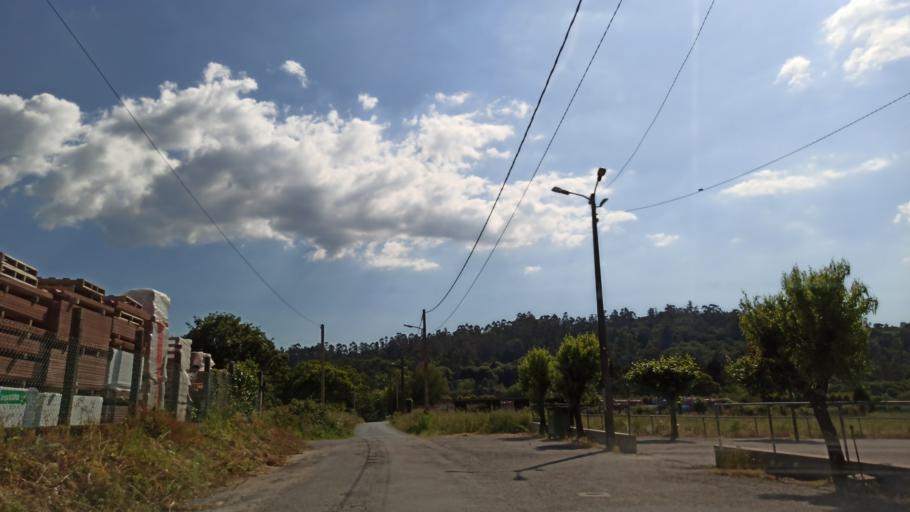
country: ES
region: Galicia
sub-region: Provincia da Coruna
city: Negreira
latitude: 42.9122
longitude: -8.7430
